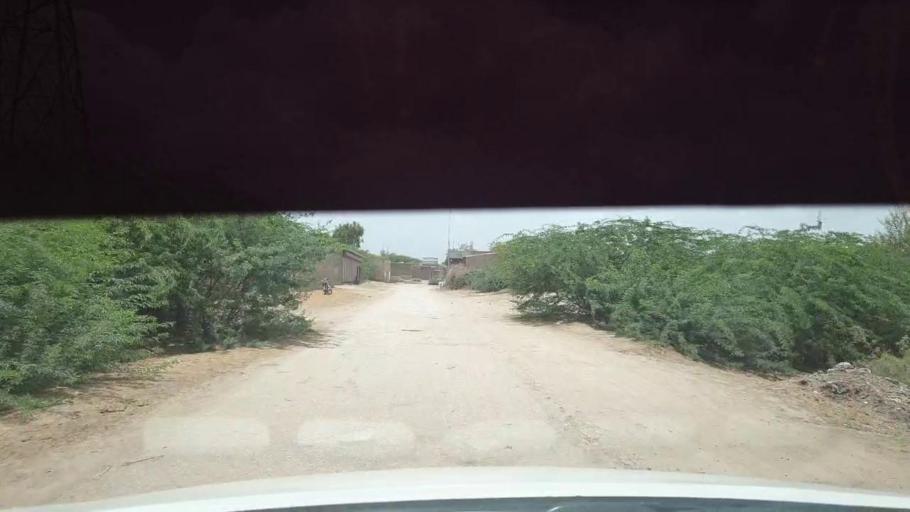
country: PK
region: Sindh
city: Kadhan
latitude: 24.4818
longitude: 68.9926
